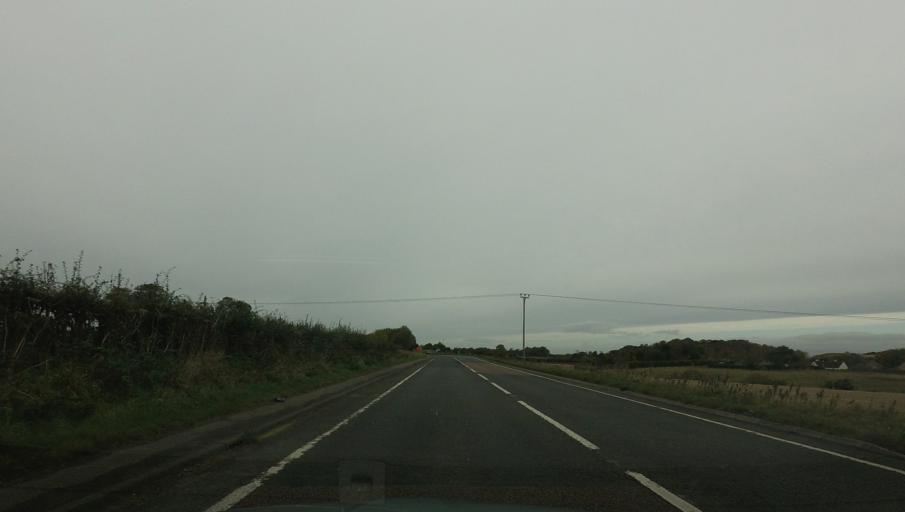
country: GB
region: Scotland
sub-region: Fife
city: Rosyth
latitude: 56.0356
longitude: -3.4488
